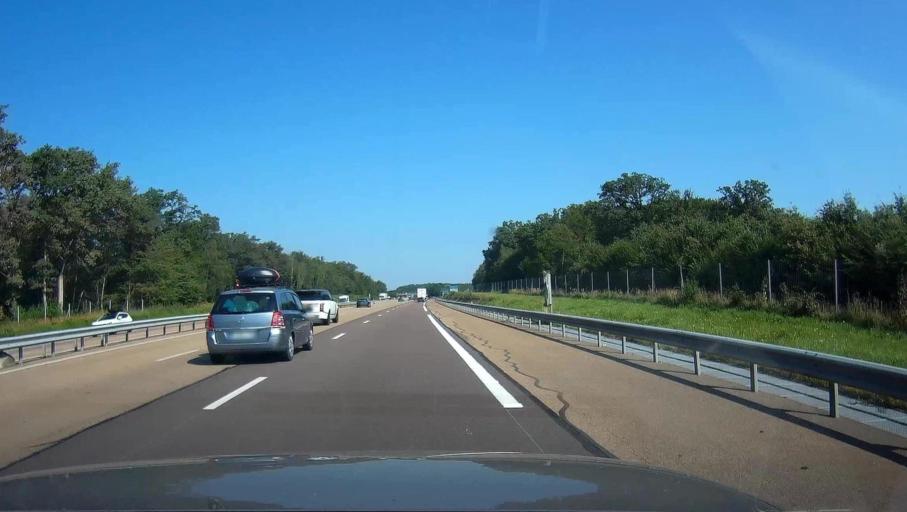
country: FR
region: Bourgogne
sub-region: Departement de la Cote-d'Or
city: Saint-Julien
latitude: 47.4145
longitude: 5.1765
